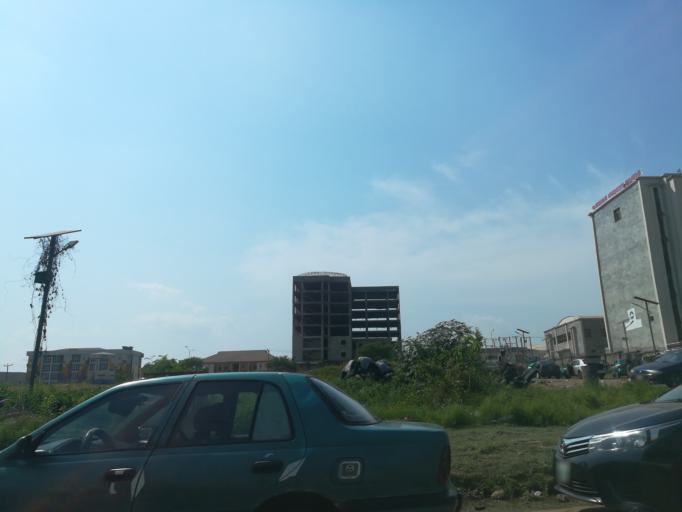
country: NG
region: Abuja Federal Capital Territory
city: Abuja
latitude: 9.0689
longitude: 7.4348
